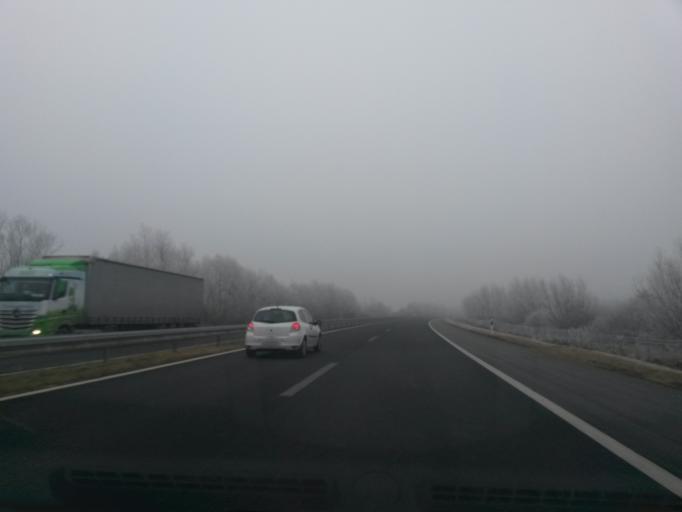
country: HR
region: Zagrebacka
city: Brckovljani
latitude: 45.9460
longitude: 16.2706
